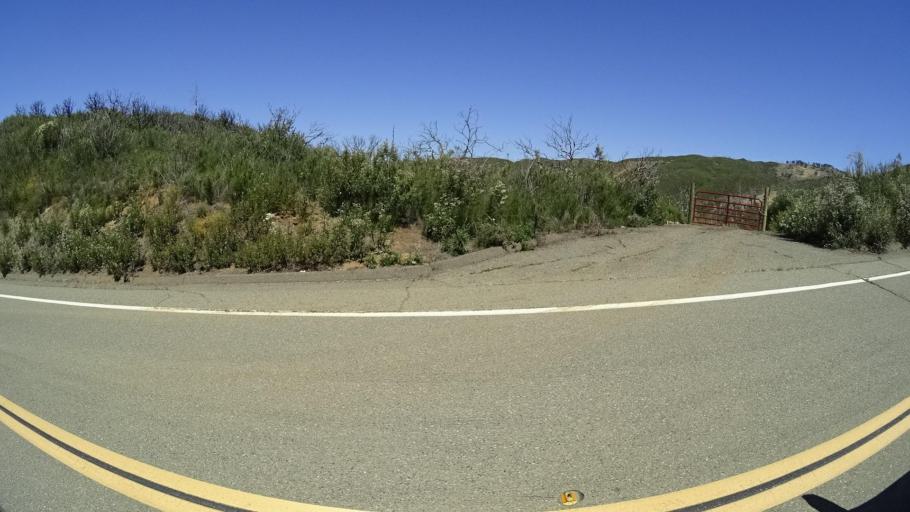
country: US
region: California
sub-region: Lake County
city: Hidden Valley Lake
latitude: 38.8886
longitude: -122.4994
